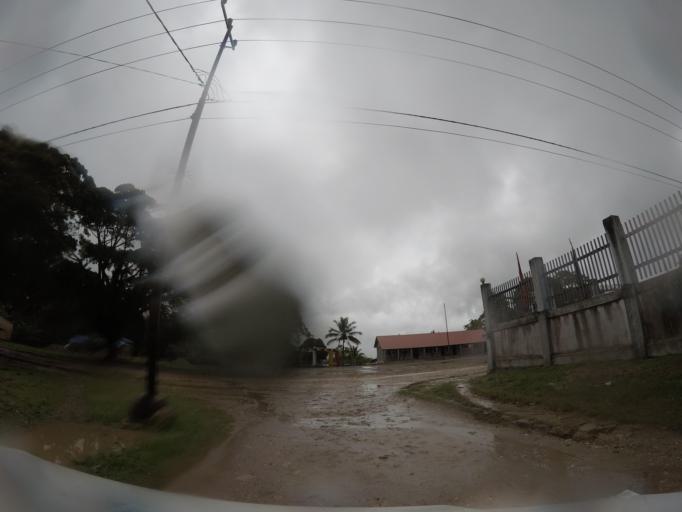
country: TL
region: Baucau
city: Venilale
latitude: -8.6432
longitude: 126.3790
